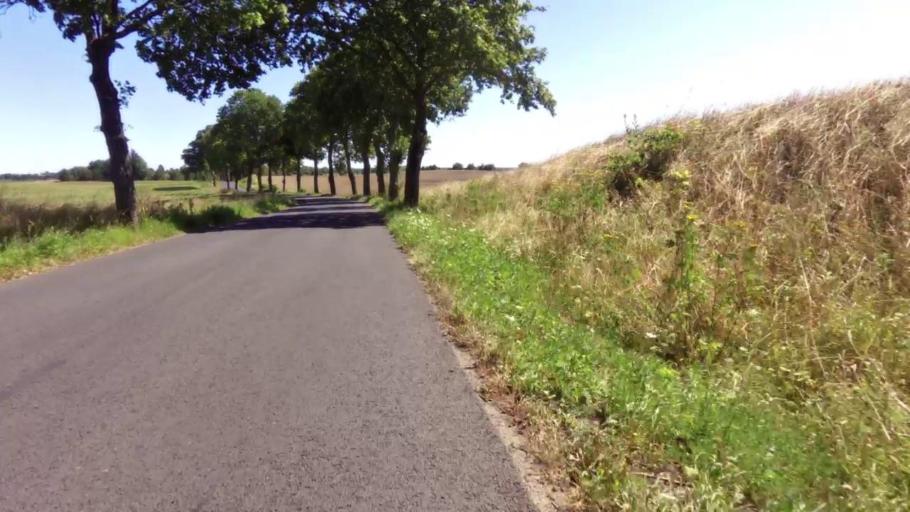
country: PL
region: West Pomeranian Voivodeship
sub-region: Powiat drawski
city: Czaplinek
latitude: 53.5584
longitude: 16.3070
